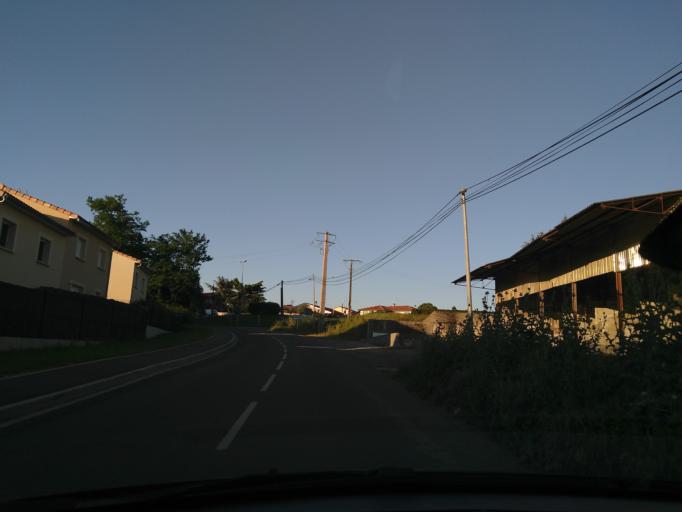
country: FR
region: Midi-Pyrenees
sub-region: Departement de la Haute-Garonne
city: Merville
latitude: 43.7256
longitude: 1.2976
